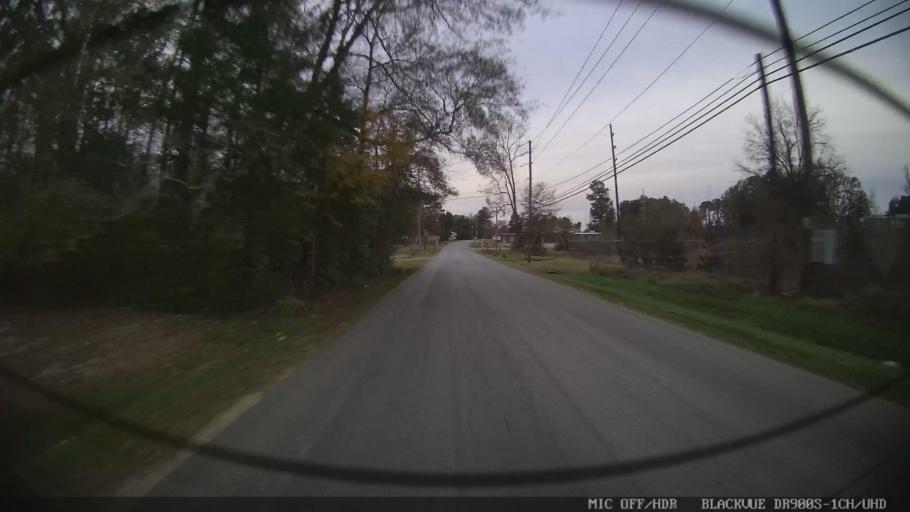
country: US
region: Mississippi
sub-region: Clarke County
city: Quitman
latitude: 32.0397
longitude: -88.7325
